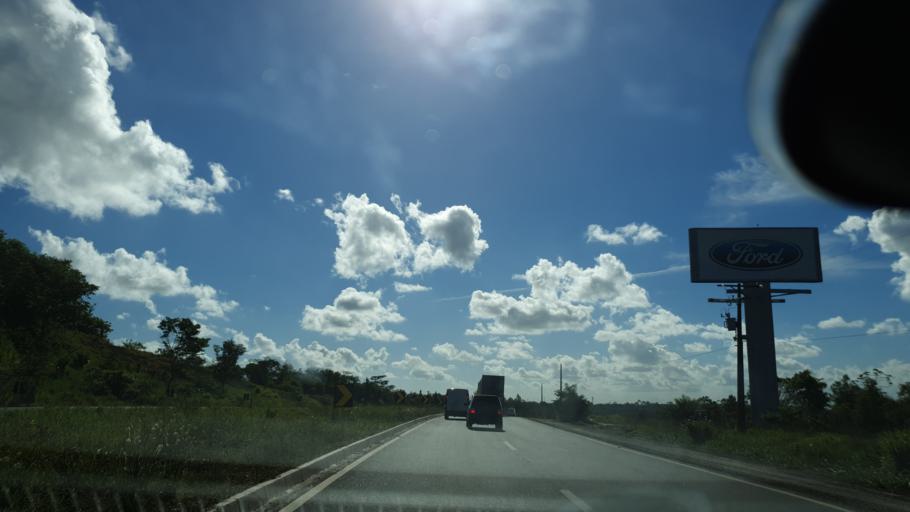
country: BR
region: Bahia
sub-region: Camacari
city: Camacari
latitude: -12.6821
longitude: -38.2891
